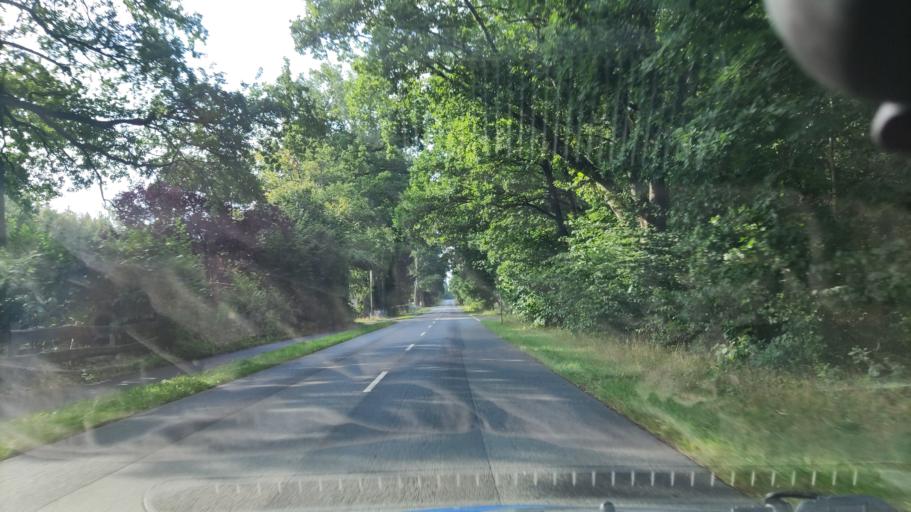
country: DE
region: Lower Saxony
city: Fassberg
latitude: 52.9641
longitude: 10.1764
